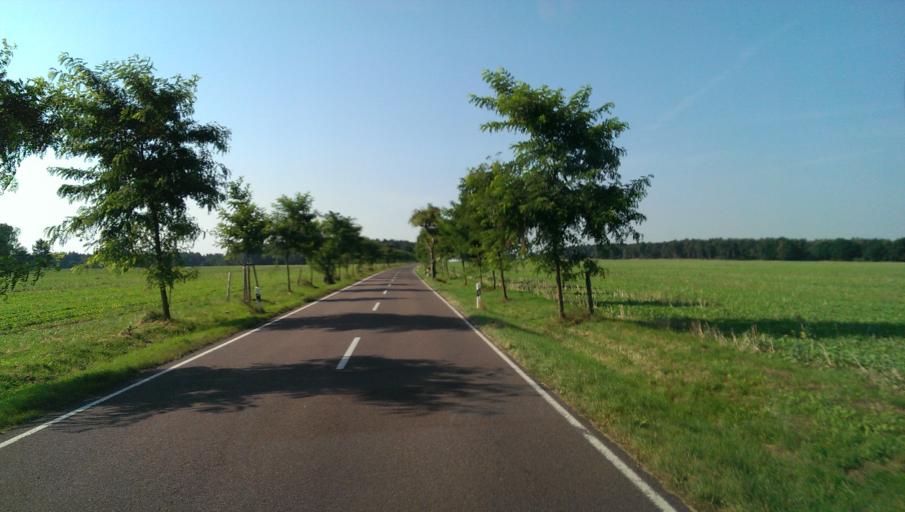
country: DE
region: Saxony-Anhalt
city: Nudersdorf
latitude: 51.9771
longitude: 12.6574
